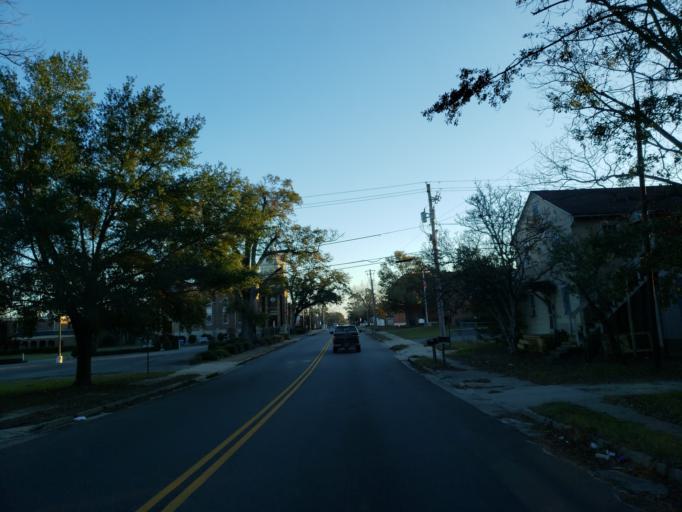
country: US
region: Georgia
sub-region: Crisp County
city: Cordele
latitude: 31.9689
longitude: -83.7796
